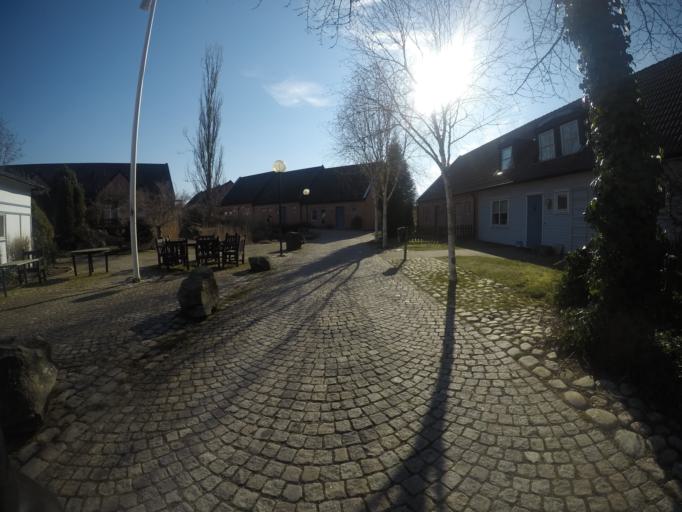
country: SE
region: Halland
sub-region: Laholms Kommun
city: Laholm
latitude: 56.5040
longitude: 13.0597
